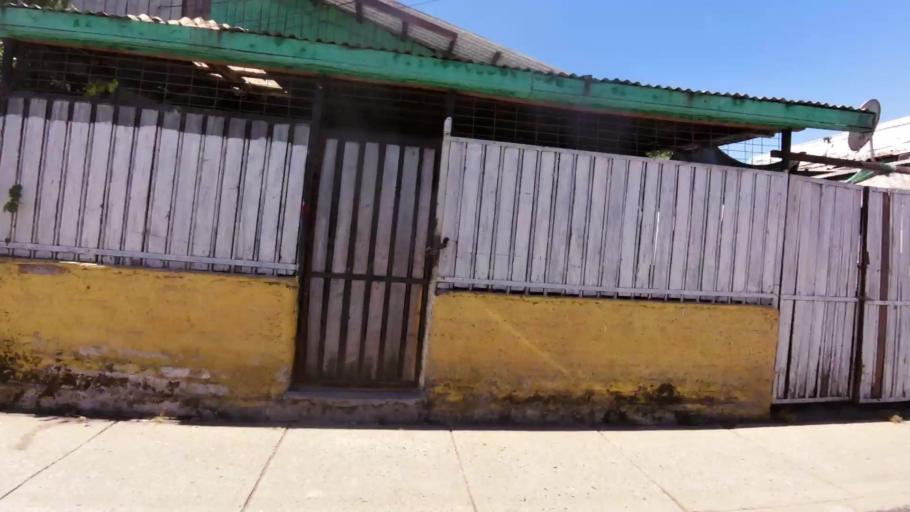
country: CL
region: O'Higgins
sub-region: Provincia de Colchagua
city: Chimbarongo
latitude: -34.5733
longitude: -70.9857
